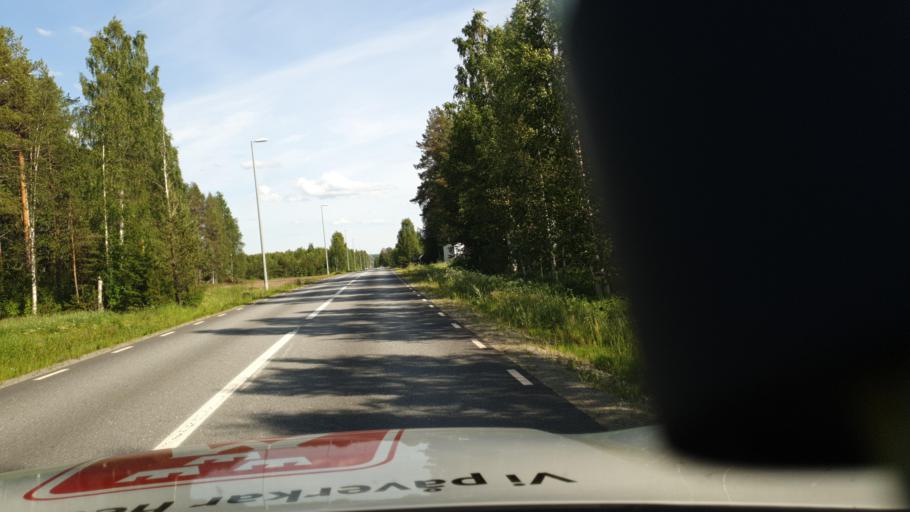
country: SE
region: Vaesterbotten
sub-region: Skelleftea Kommun
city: Forsbacka
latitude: 64.6939
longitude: 20.4936
